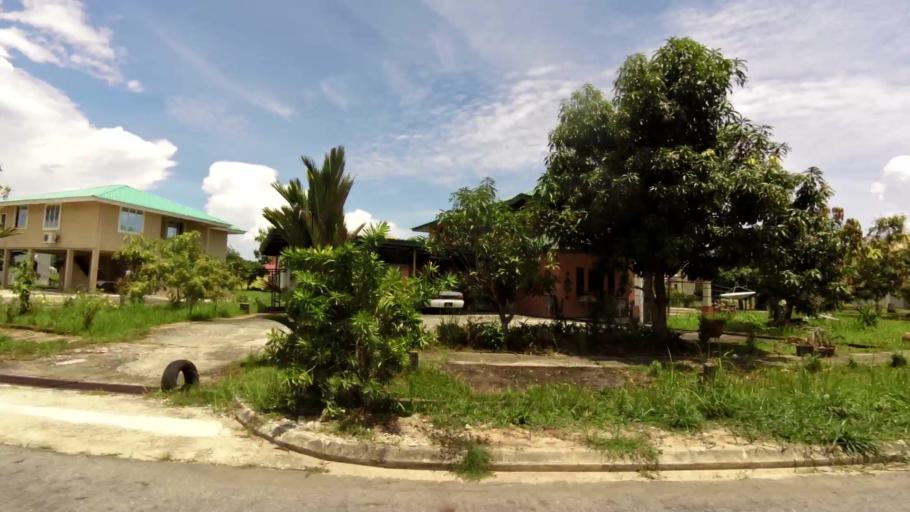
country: BN
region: Brunei and Muara
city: Bandar Seri Begawan
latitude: 4.9605
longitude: 114.9150
